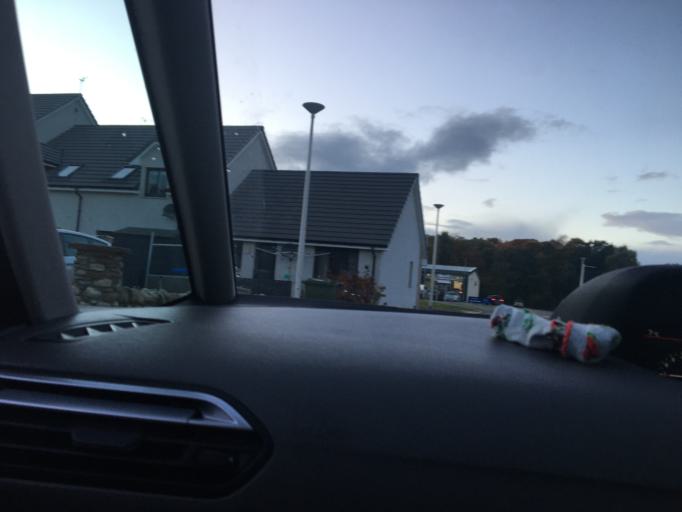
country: GB
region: Scotland
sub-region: Highland
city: Beauly
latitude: 57.3292
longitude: -4.4764
